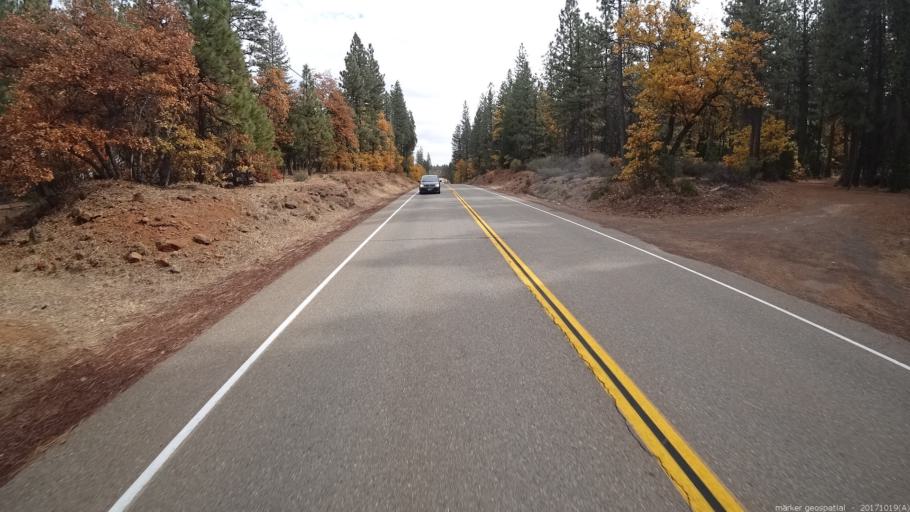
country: US
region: California
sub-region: Shasta County
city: Burney
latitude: 41.0974
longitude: -121.5570
